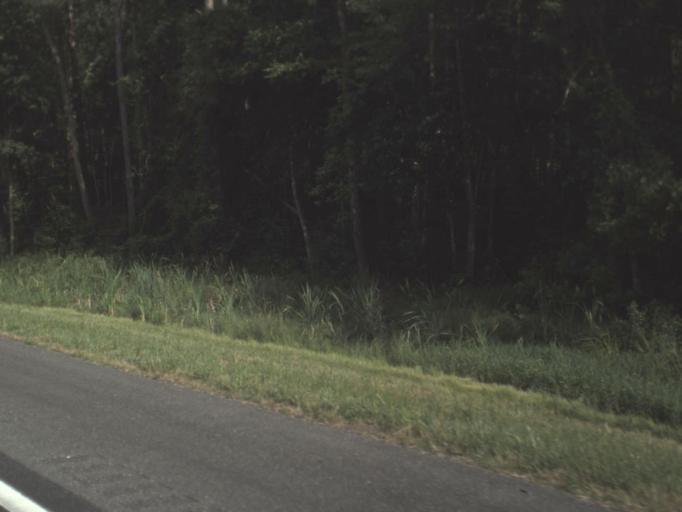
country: US
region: Florida
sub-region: Baker County
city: Macclenny
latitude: 30.2541
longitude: -82.2002
